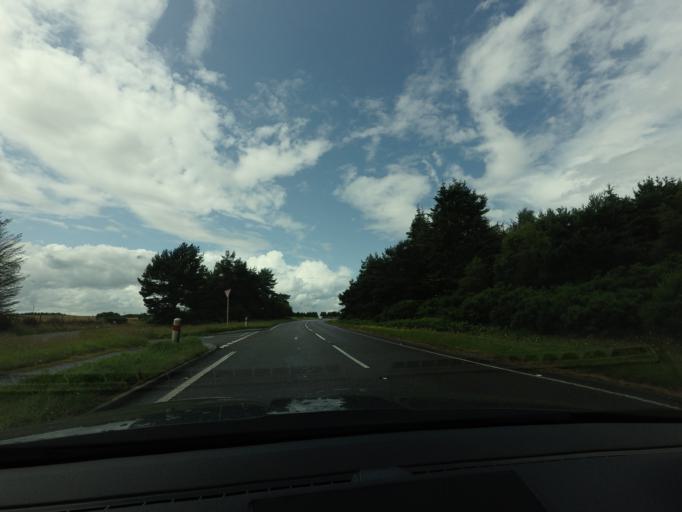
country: GB
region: Scotland
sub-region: Moray
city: Lhanbryd
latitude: 57.6278
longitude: -3.1674
